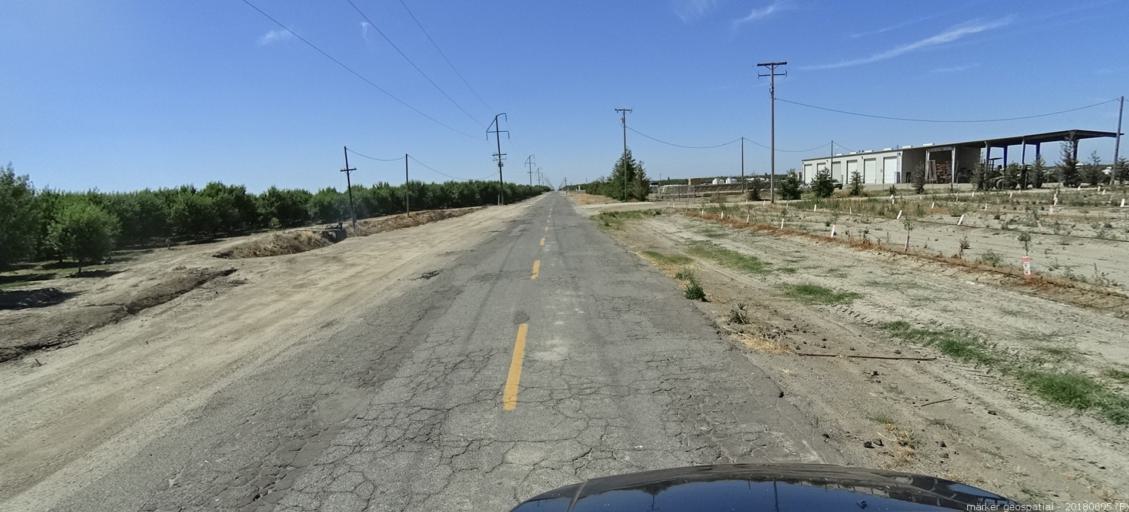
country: US
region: California
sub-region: Madera County
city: Chowchilla
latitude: 37.1168
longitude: -120.3471
